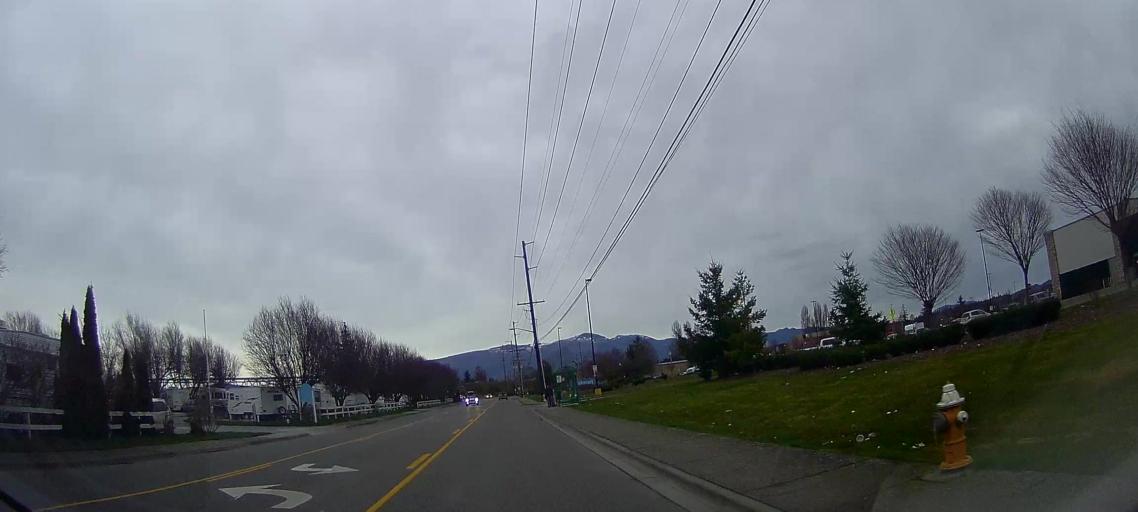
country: US
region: Washington
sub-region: Skagit County
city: Mount Vernon
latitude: 48.4432
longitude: -122.3459
